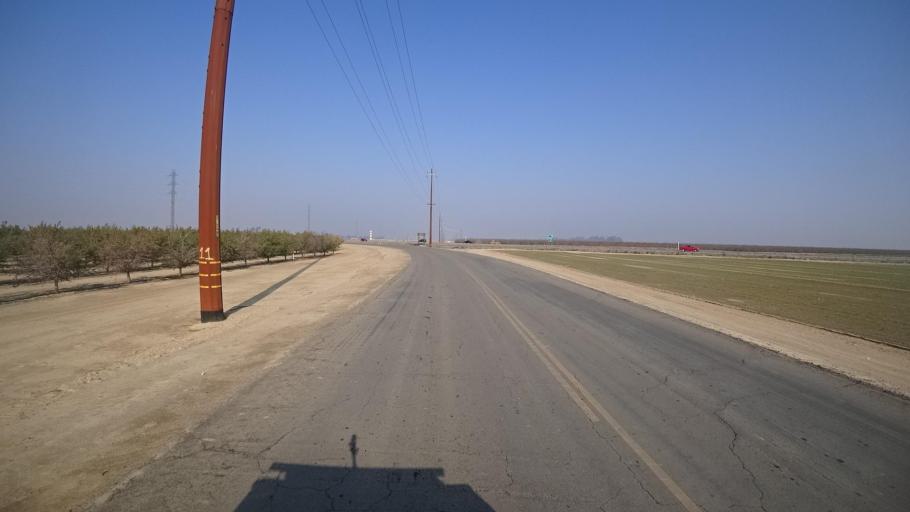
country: US
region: California
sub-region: Kern County
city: Buttonwillow
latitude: 35.4335
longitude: -119.4470
